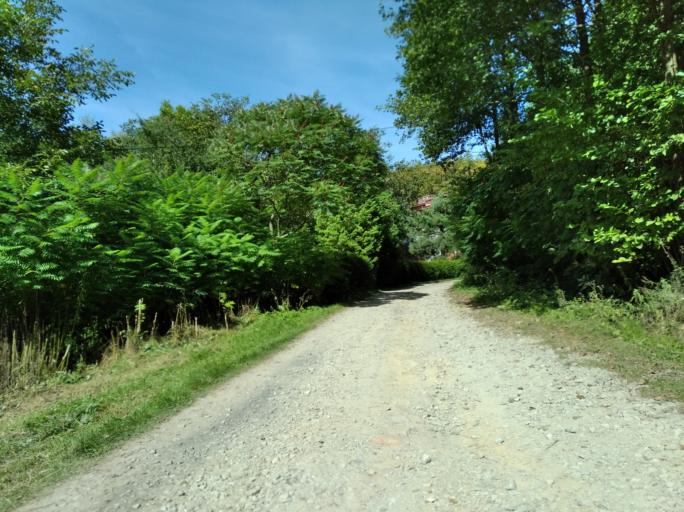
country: PL
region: Subcarpathian Voivodeship
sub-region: Powiat ropczycko-sedziszowski
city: Wielopole Skrzynskie
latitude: 49.9132
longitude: 21.6267
